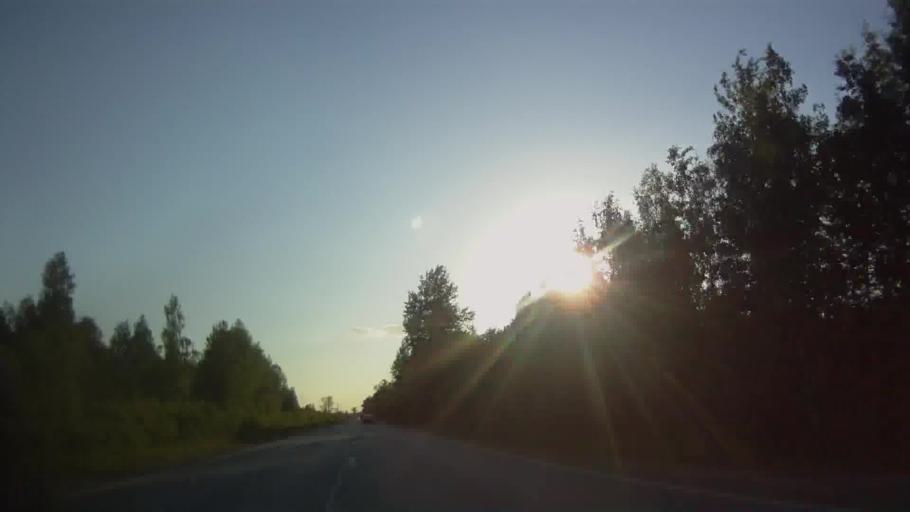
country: LV
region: Livani
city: Livani
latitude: 56.5312
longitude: 26.3492
